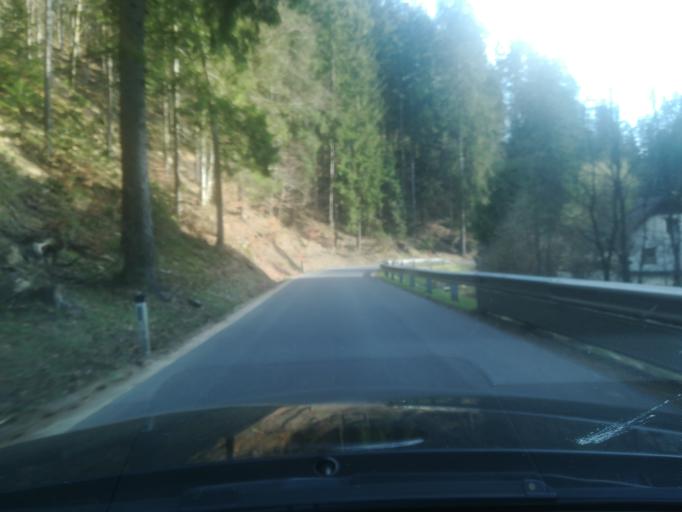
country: AT
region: Upper Austria
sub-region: Politischer Bezirk Freistadt
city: Freistadt
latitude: 48.4170
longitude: 14.6387
